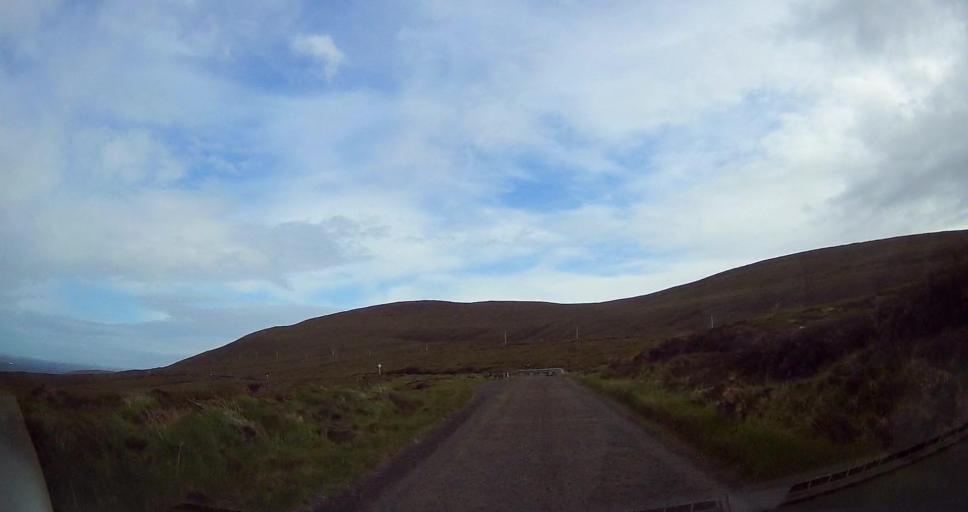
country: GB
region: Scotland
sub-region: Orkney Islands
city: Stromness
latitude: 58.8973
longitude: -3.2733
